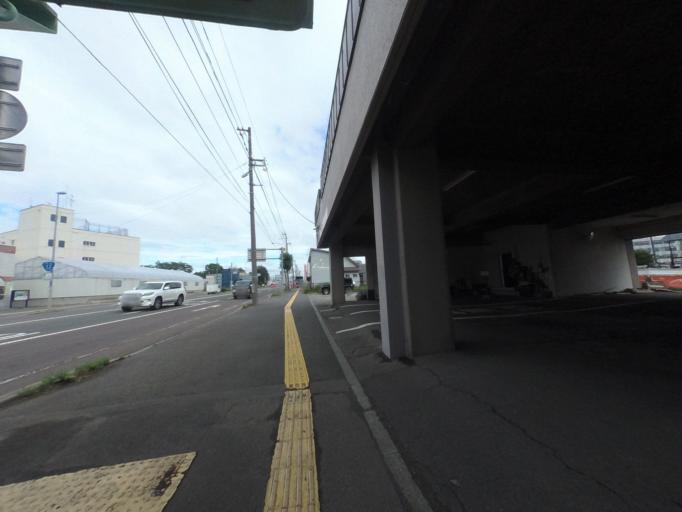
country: JP
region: Hokkaido
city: Sapporo
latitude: 43.0618
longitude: 141.3855
